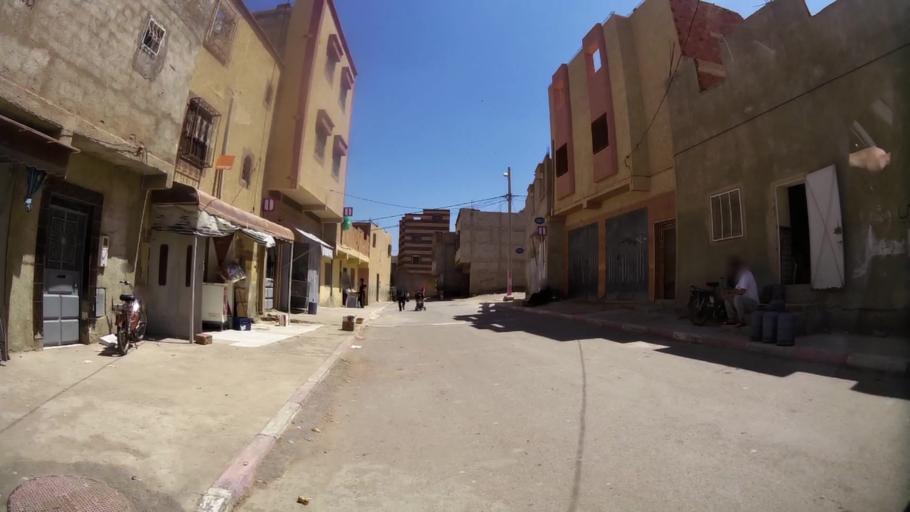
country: MA
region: Oriental
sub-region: Oujda-Angad
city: Oujda
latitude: 34.6784
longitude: -1.9542
